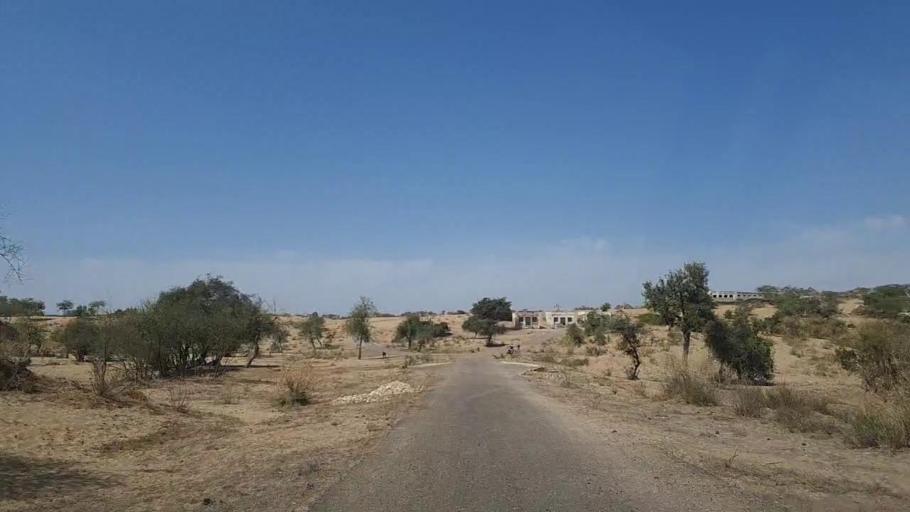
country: PK
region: Sindh
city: Mithi
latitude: 24.8675
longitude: 69.6609
